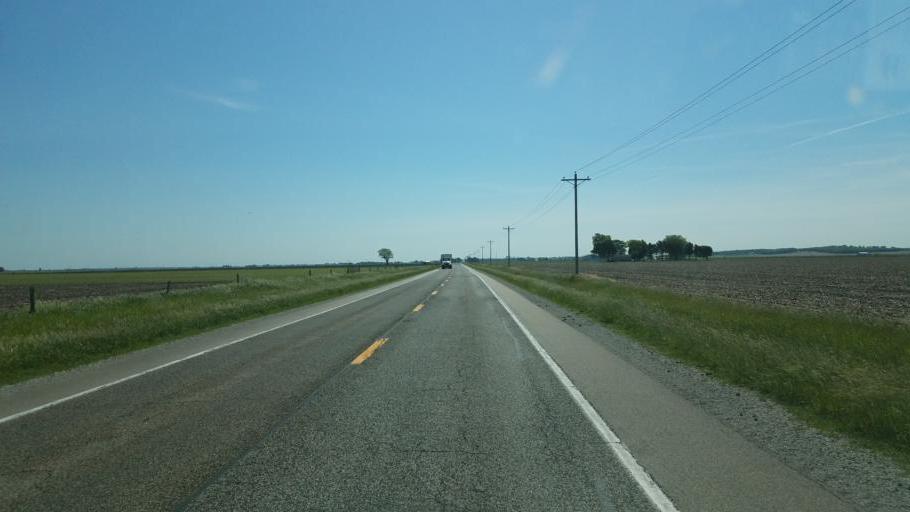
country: US
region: Illinois
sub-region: Mason County
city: Mason City
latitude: 40.3044
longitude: -89.7288
